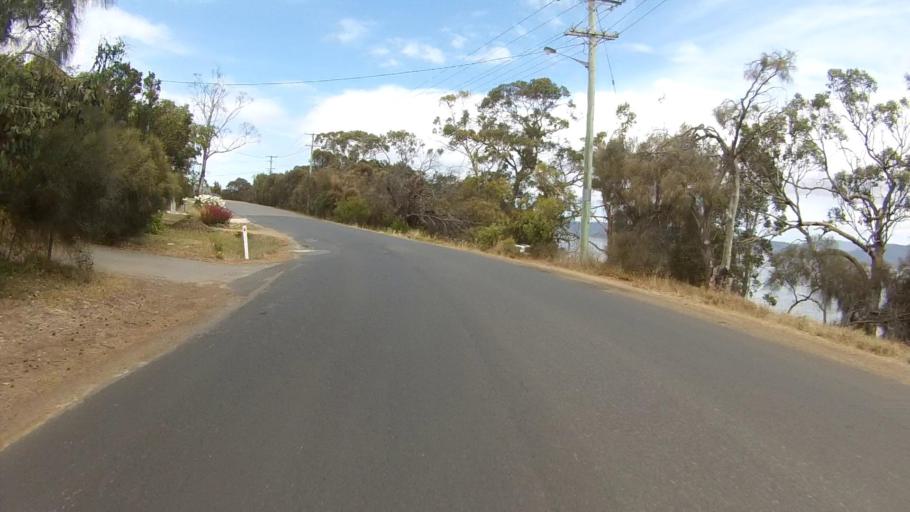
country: AU
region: Tasmania
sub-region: Kingborough
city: Margate
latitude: -43.0260
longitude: 147.2910
